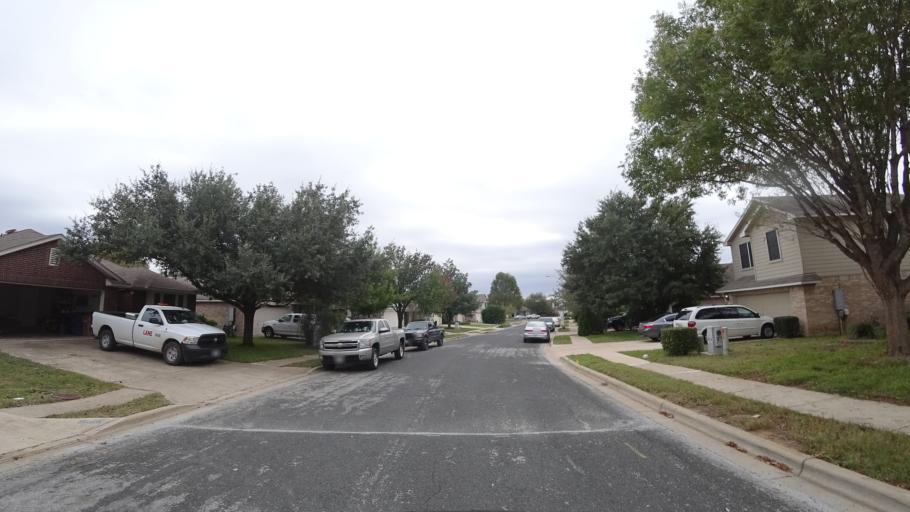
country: US
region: Texas
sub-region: Travis County
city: Shady Hollow
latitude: 30.1510
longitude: -97.8509
